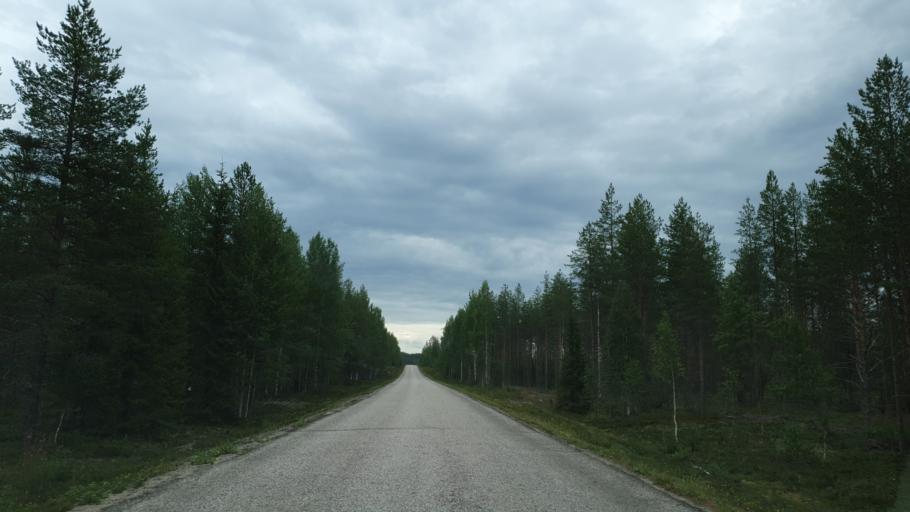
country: FI
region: Kainuu
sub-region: Kehys-Kainuu
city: Kuhmo
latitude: 64.3416
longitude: 29.3065
